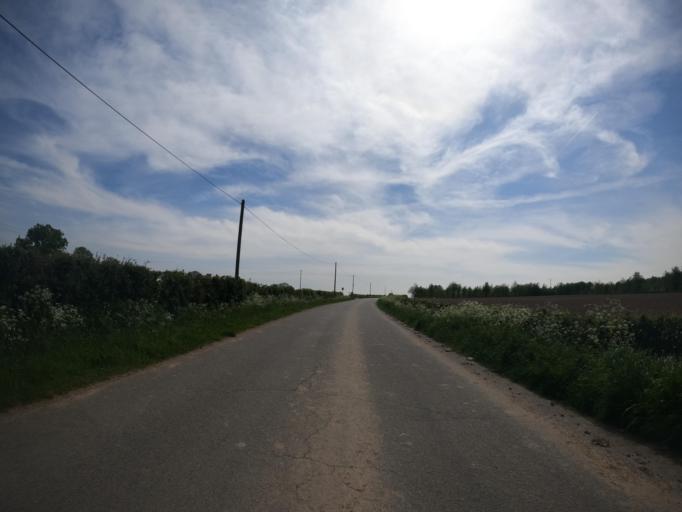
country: FR
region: Poitou-Charentes
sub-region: Departement des Deux-Sevres
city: La Chapelle-Saint-Laurent
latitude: 46.6563
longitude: -0.5071
